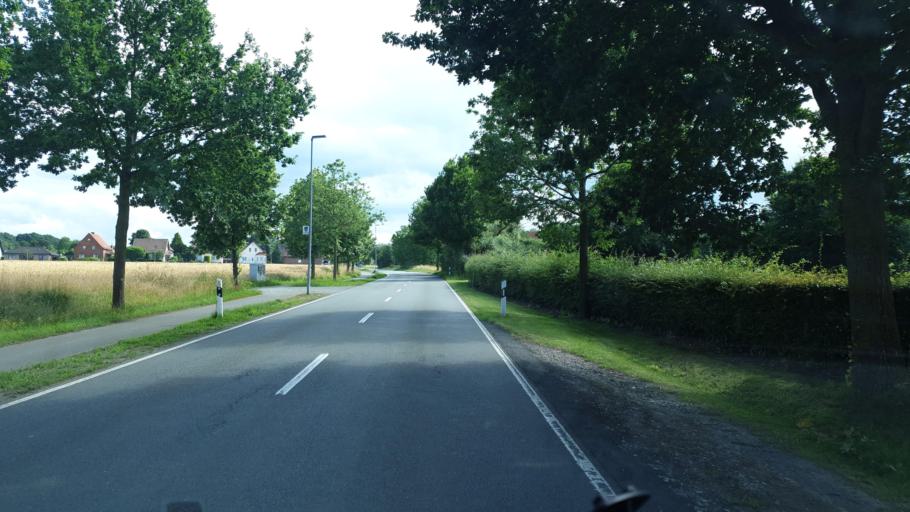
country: DE
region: North Rhine-Westphalia
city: Bad Oeynhausen
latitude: 52.1899
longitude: 8.7821
